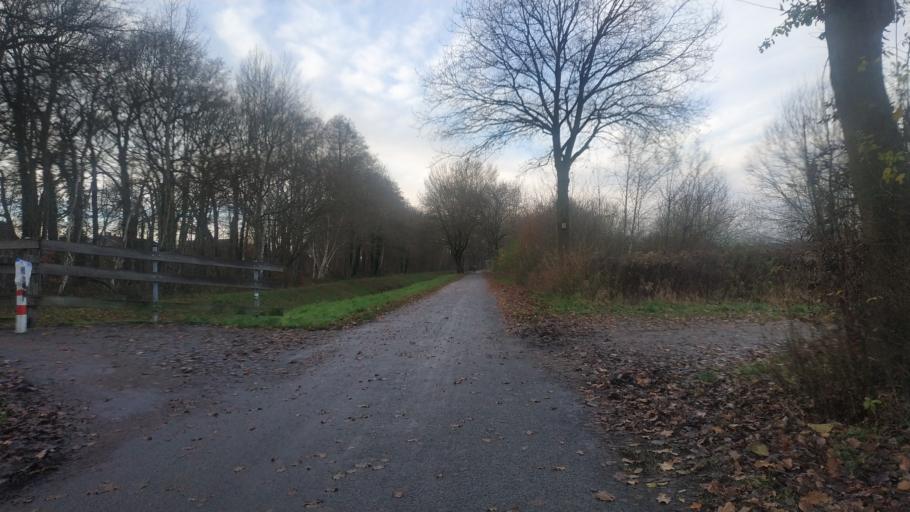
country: DE
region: North Rhine-Westphalia
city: Ibbenburen
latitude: 52.2760
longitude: 7.6893
